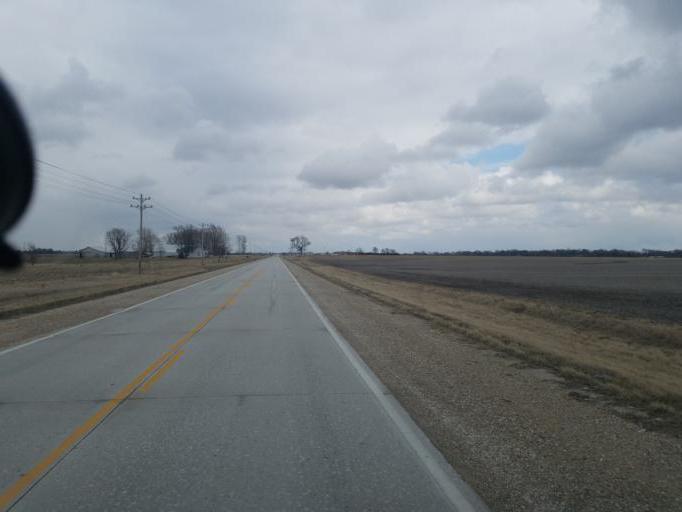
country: US
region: Missouri
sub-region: Boone County
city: Hallsville
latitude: 39.2458
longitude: -92.2975
